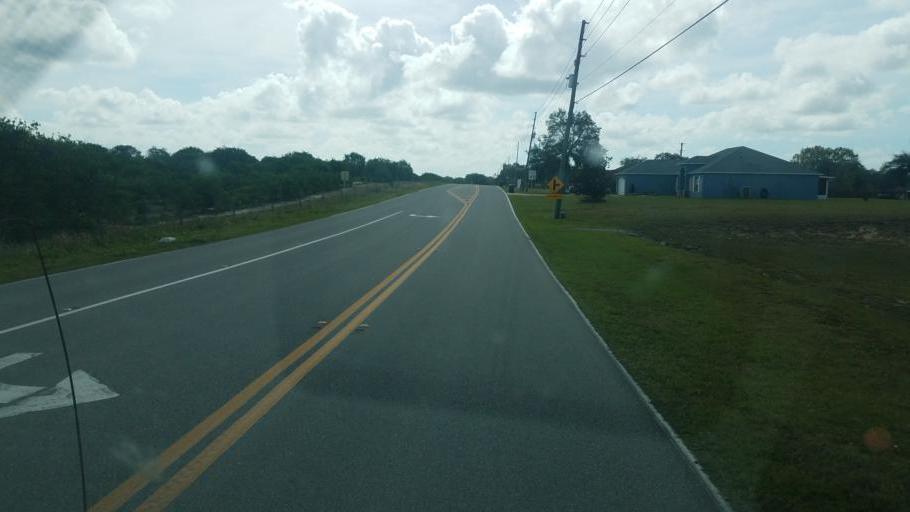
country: US
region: Florida
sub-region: Polk County
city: Dundee
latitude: 28.0247
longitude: -81.5292
